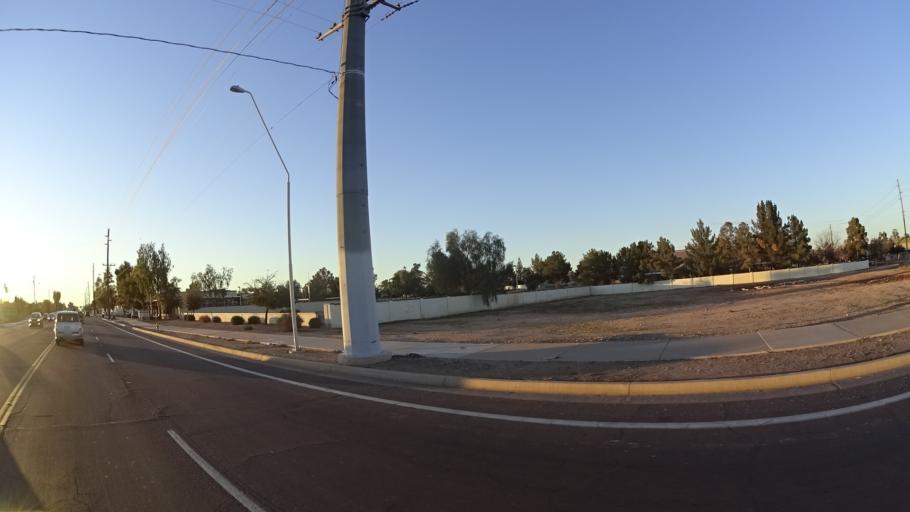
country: US
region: Arizona
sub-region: Maricopa County
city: Tempe
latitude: 33.4221
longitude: -111.8834
